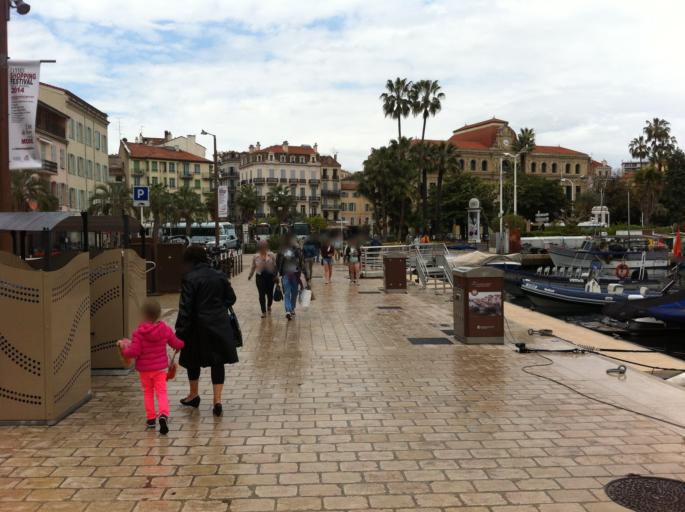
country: FR
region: Provence-Alpes-Cote d'Azur
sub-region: Departement des Alpes-Maritimes
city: Cannes
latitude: 43.5501
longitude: 7.0123
